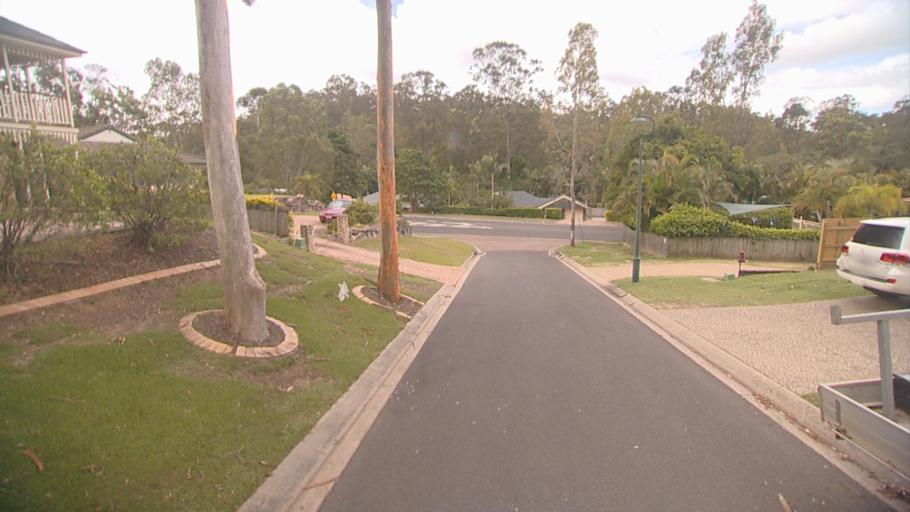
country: AU
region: Queensland
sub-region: Logan
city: Slacks Creek
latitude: -27.6576
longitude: 153.1966
